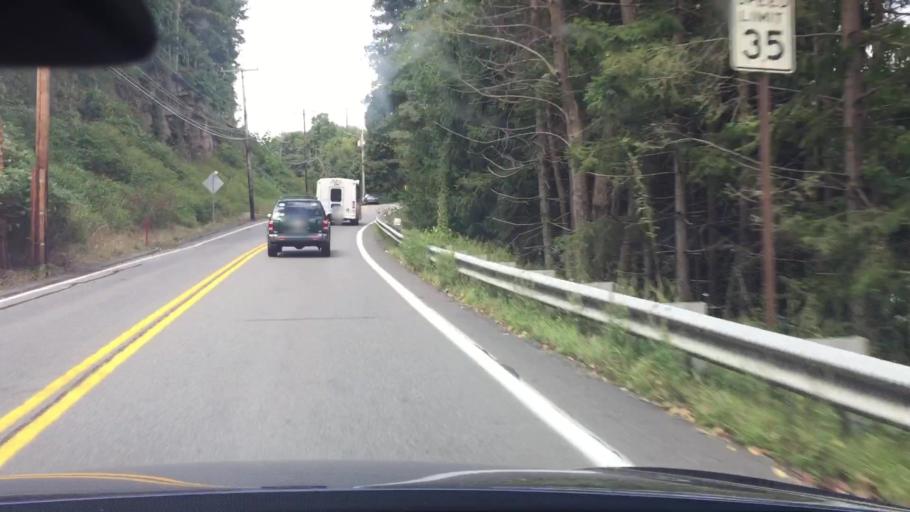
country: US
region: Pennsylvania
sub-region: Allegheny County
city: Cheswick
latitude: 40.5114
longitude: -79.8006
